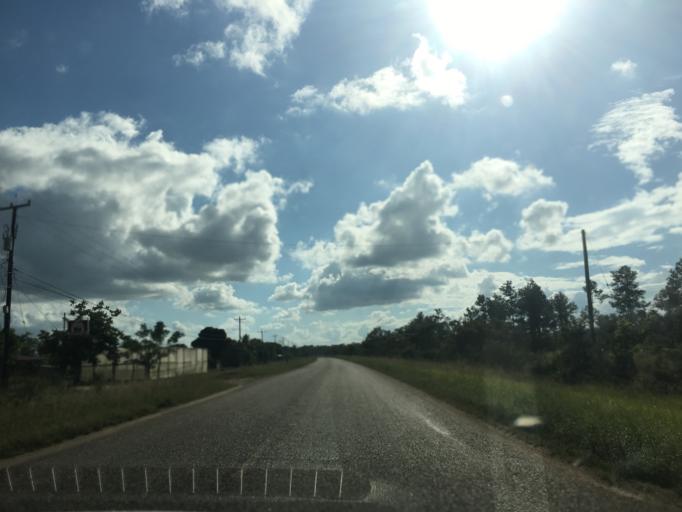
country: BZ
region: Stann Creek
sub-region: Dangriga
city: Dangriga
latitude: 16.8766
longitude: -88.3450
